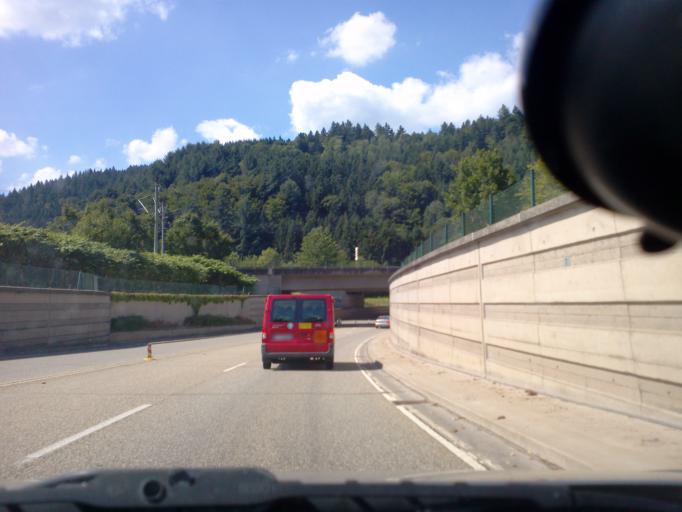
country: DE
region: Baden-Wuerttemberg
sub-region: Freiburg Region
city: Hausach
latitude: 48.2848
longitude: 8.1549
